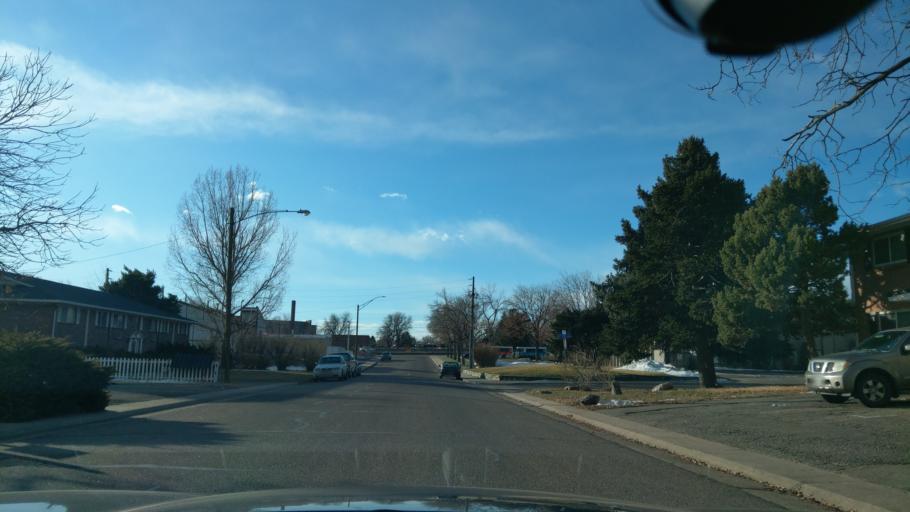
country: US
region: Colorado
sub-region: Jefferson County
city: Lakewood
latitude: 39.7275
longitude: -105.1149
